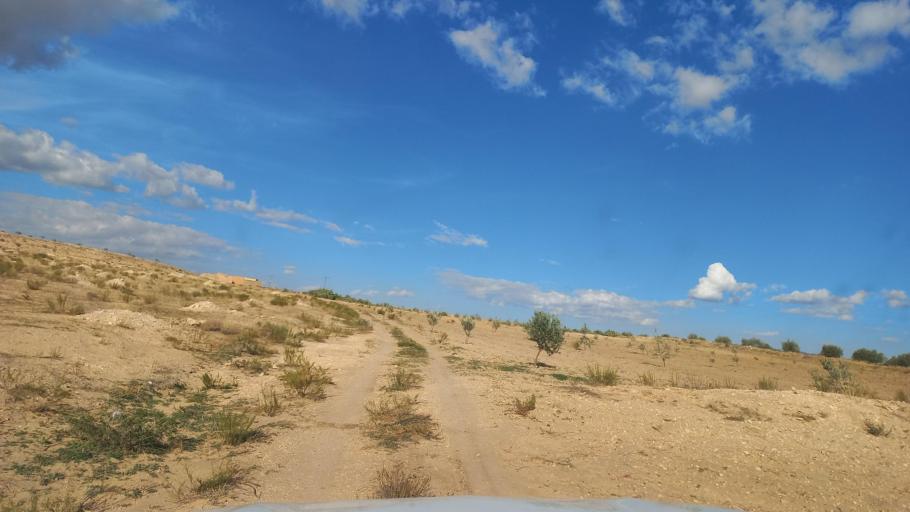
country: TN
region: Al Qasrayn
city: Sbiba
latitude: 35.3988
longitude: 9.0143
